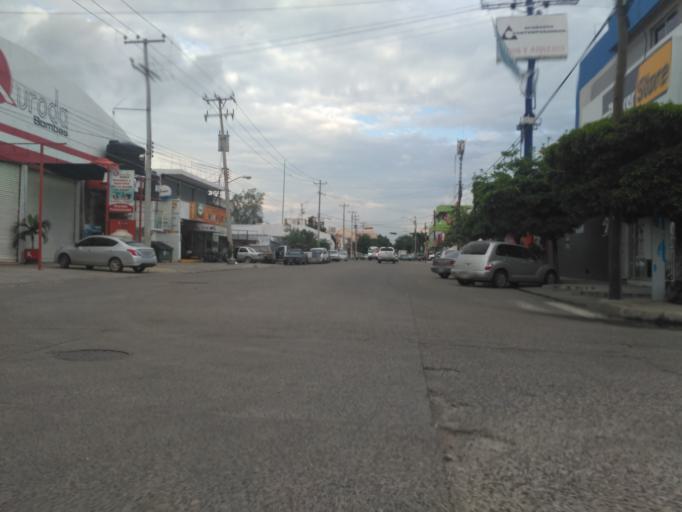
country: MX
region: Sinaloa
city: Culiacan
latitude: 24.7977
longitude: -107.4029
